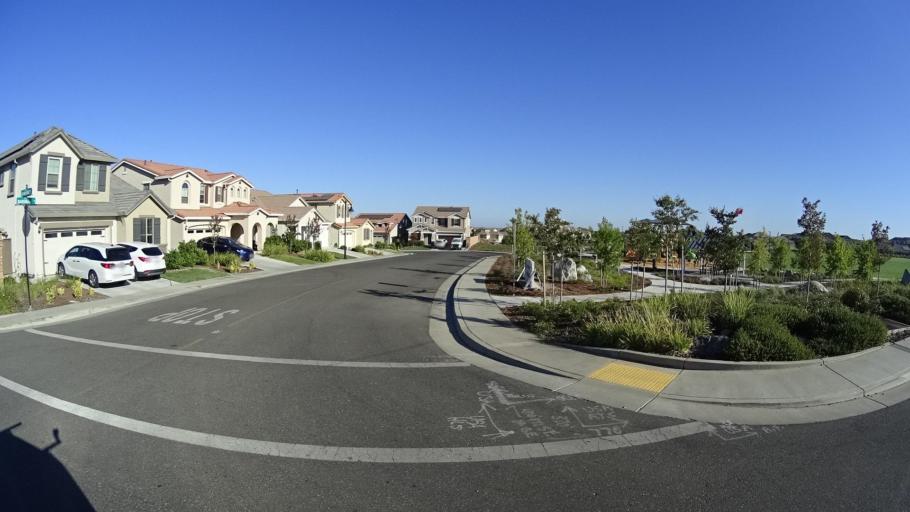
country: US
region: California
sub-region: Placer County
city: Rocklin
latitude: 38.8327
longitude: -121.2711
